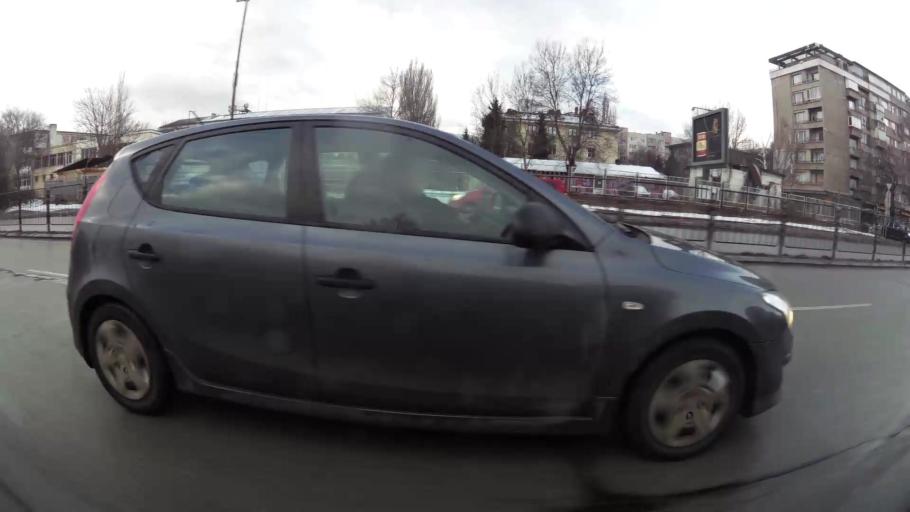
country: BG
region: Sofia-Capital
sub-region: Stolichna Obshtina
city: Sofia
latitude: 42.7047
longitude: 23.2906
